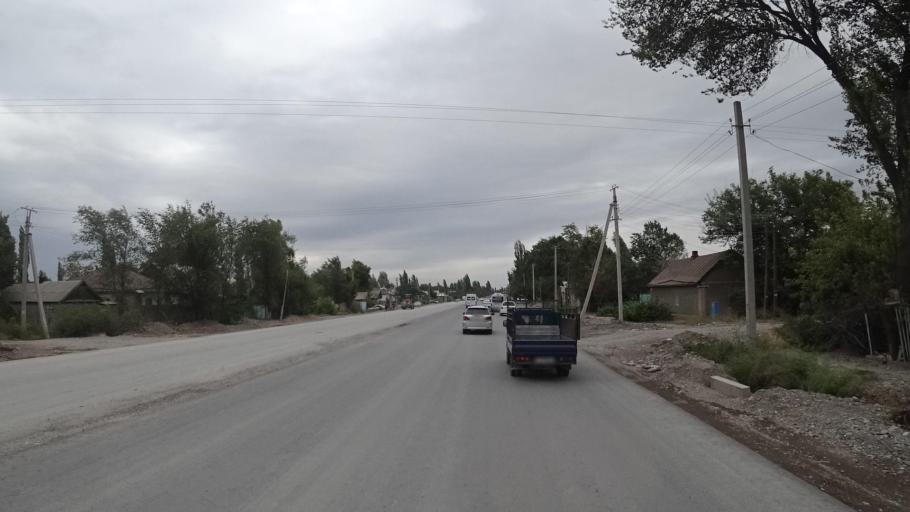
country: KG
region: Chuy
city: Belovodskoye
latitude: 42.8504
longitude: 74.1762
